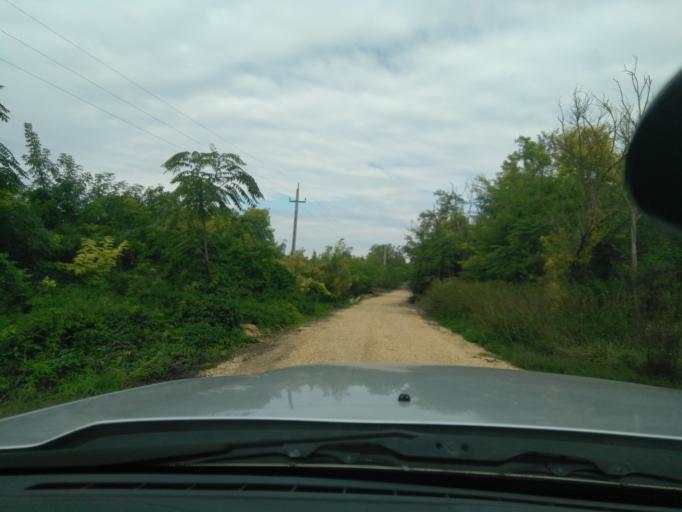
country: HU
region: Fejer
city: Val
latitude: 47.3805
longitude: 18.7410
